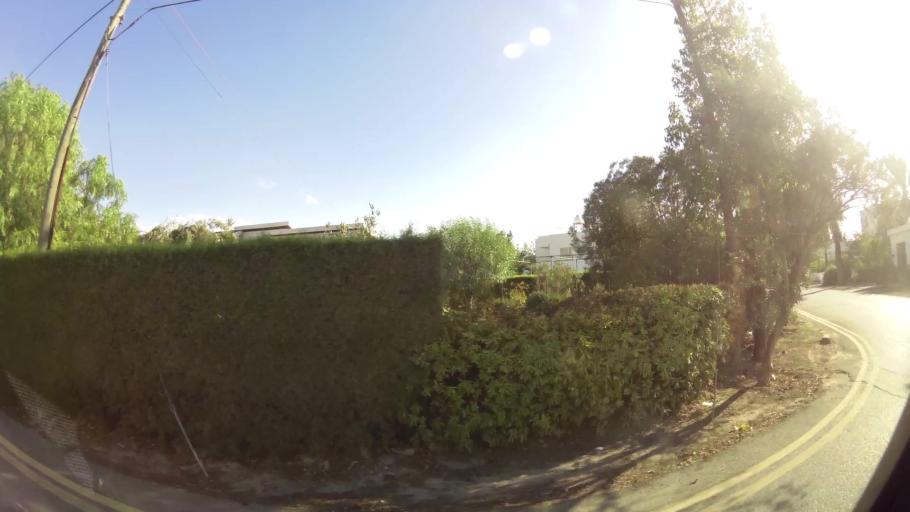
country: CY
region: Lefkosia
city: Nicosia
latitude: 35.1963
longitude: 33.3357
